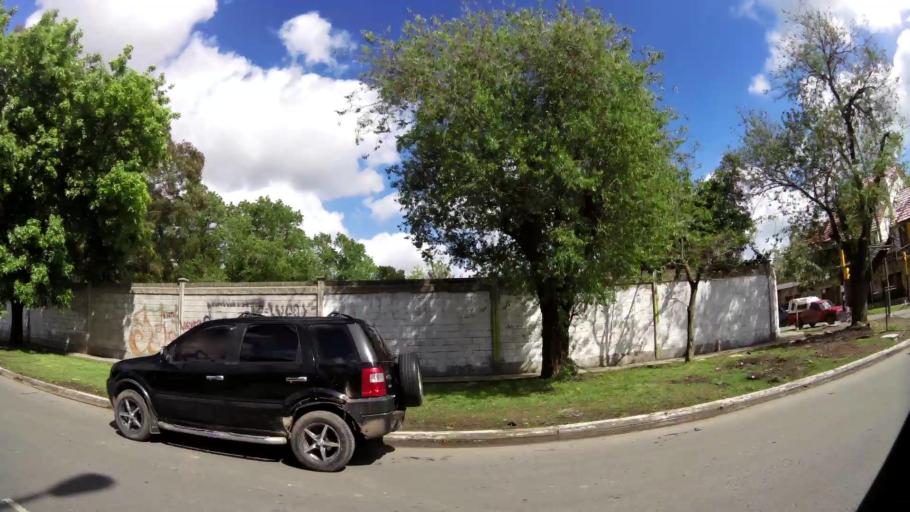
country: AR
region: Buenos Aires
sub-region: Partido de Quilmes
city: Quilmes
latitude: -34.8301
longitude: -58.1838
